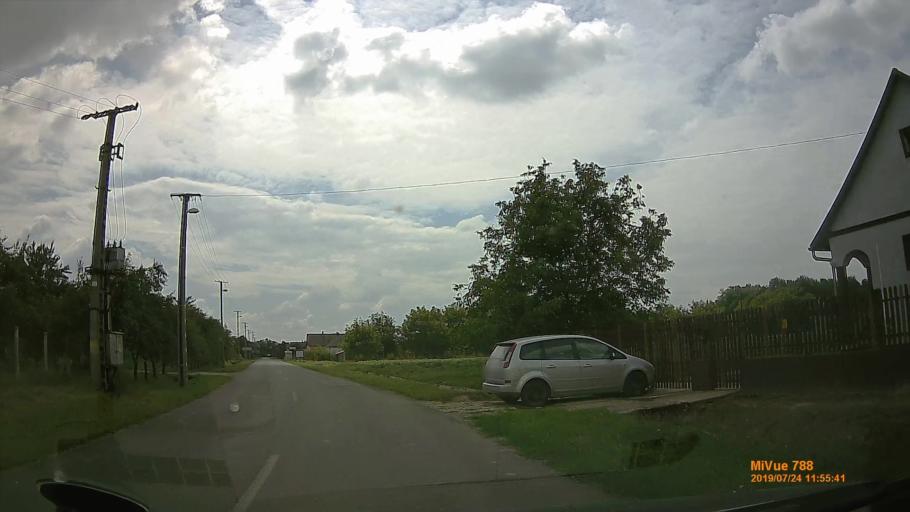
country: HU
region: Szabolcs-Szatmar-Bereg
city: Vasarosnameny
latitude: 48.2064
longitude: 22.4134
